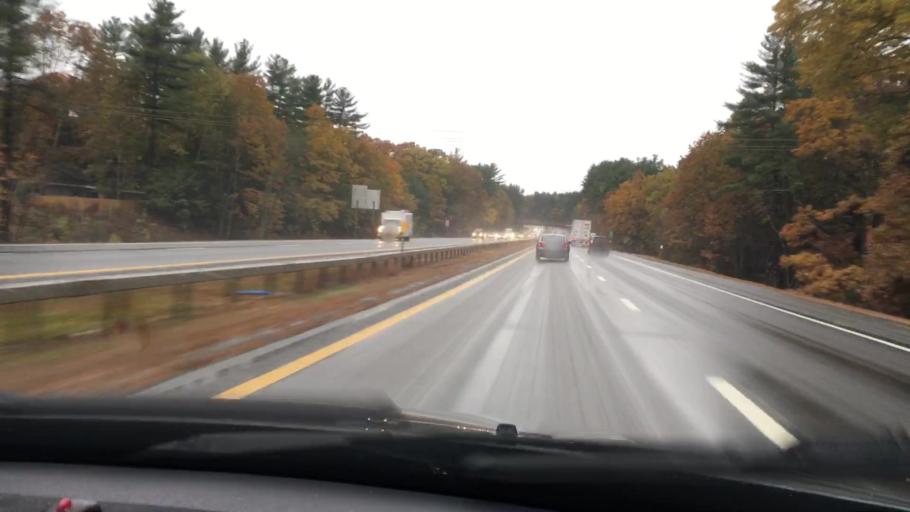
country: US
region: New Hampshire
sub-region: Hillsborough County
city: East Merrimack
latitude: 42.8770
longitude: -71.4903
